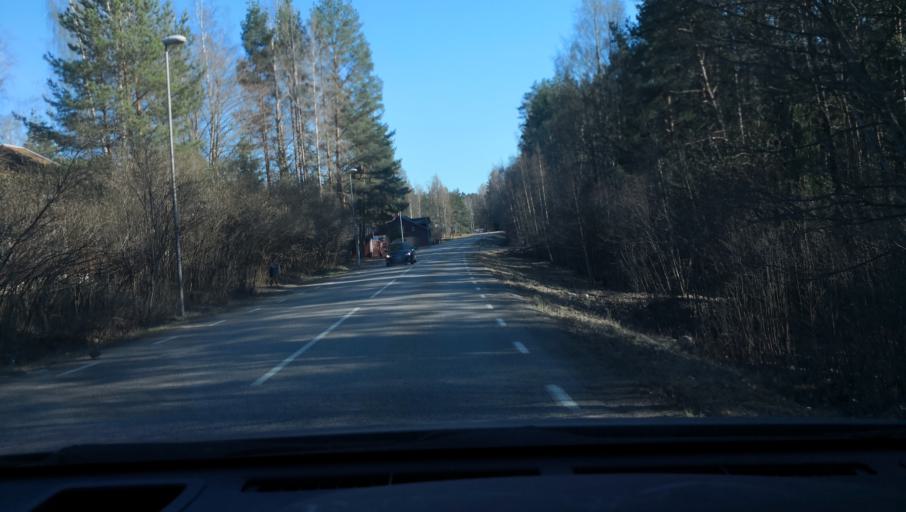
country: SE
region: Vaestmanland
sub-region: Surahammars Kommun
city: Ramnas
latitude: 59.9229
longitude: 16.3454
